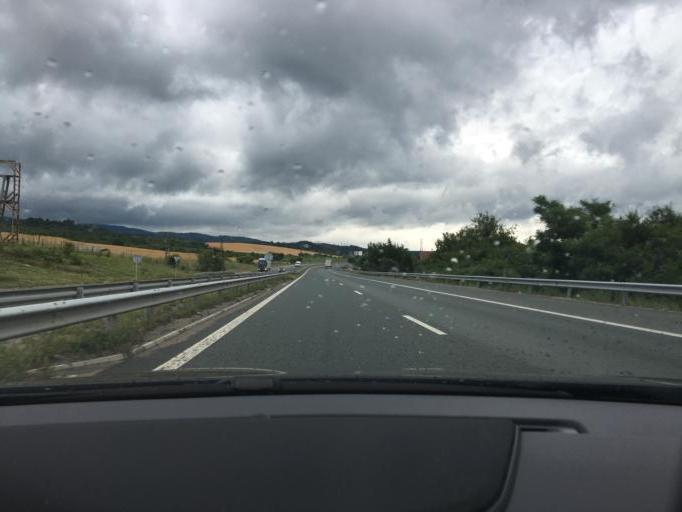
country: BG
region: Pernik
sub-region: Obshtina Pernik
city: Pernik
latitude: 42.5541
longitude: 23.1210
